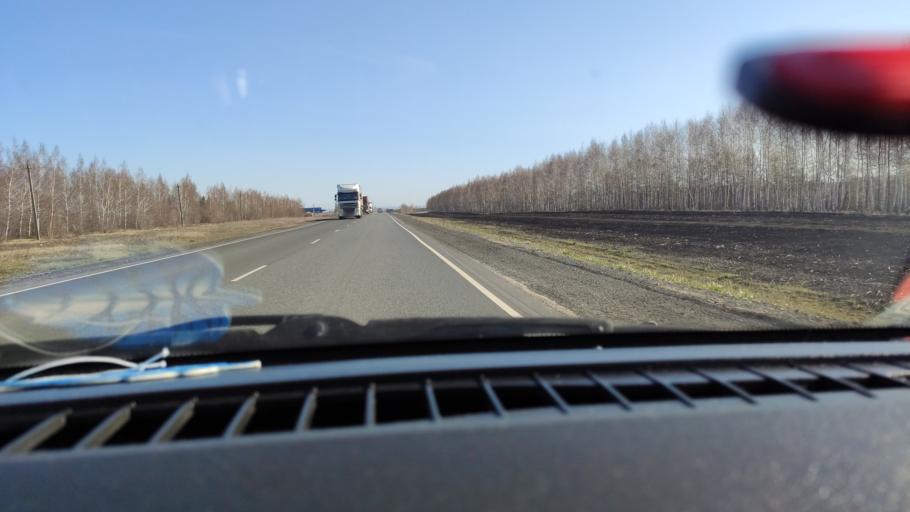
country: RU
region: Samara
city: Syzran'
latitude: 52.9924
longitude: 48.3228
